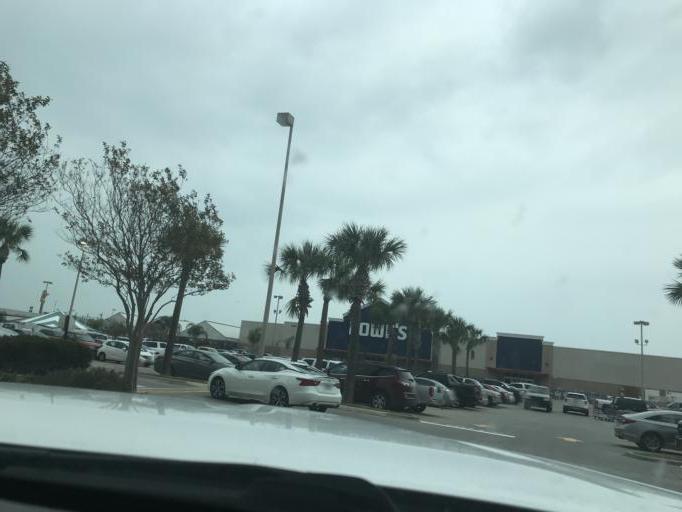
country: US
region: Texas
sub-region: Nueces County
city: Corpus Christi
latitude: 27.7008
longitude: -97.3629
